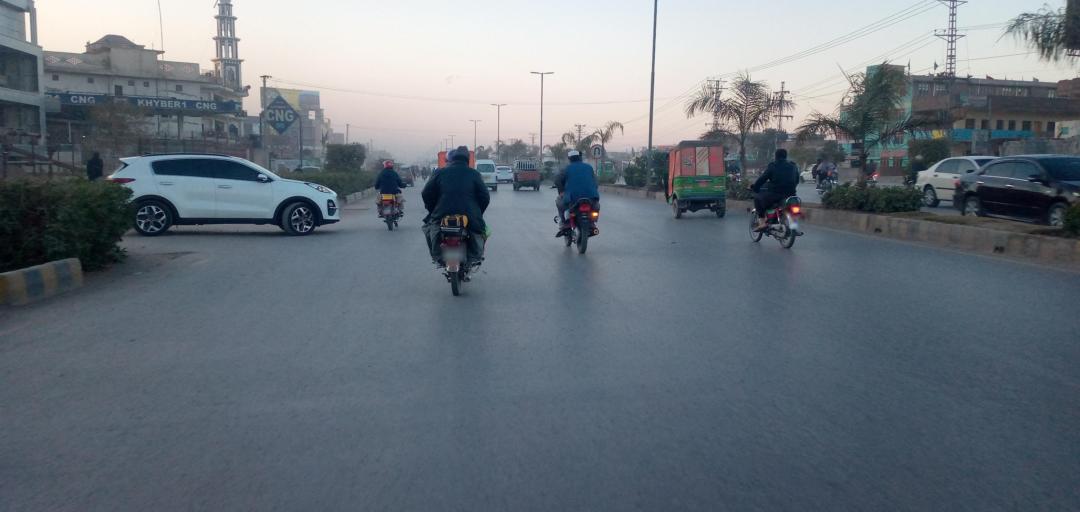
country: PK
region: Khyber Pakhtunkhwa
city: Peshawar
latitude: 34.0285
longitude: 71.6155
